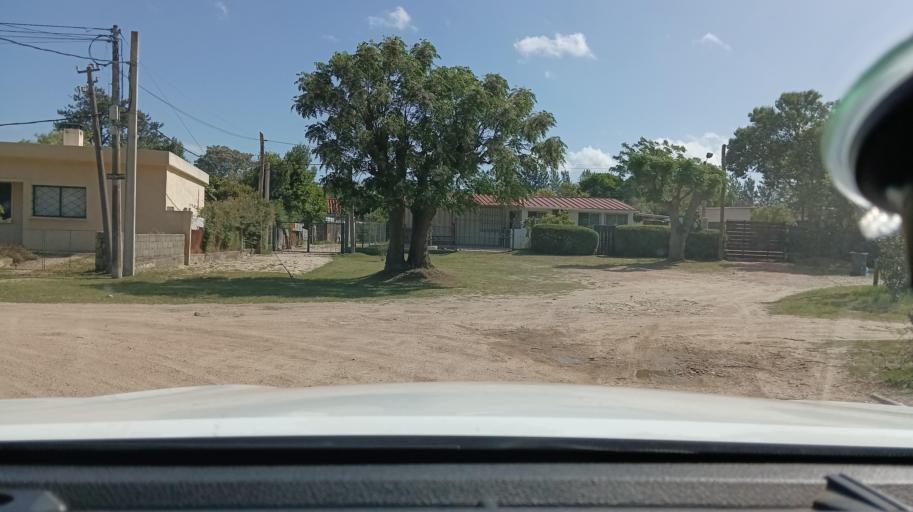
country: UY
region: Canelones
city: Paso de Carrasco
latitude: -34.8516
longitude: -56.0415
